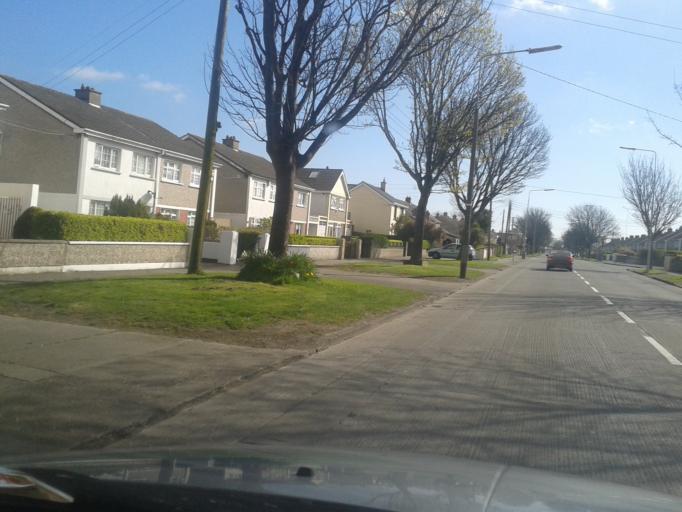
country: IE
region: Leinster
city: Raheny
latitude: 53.3907
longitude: -6.1854
